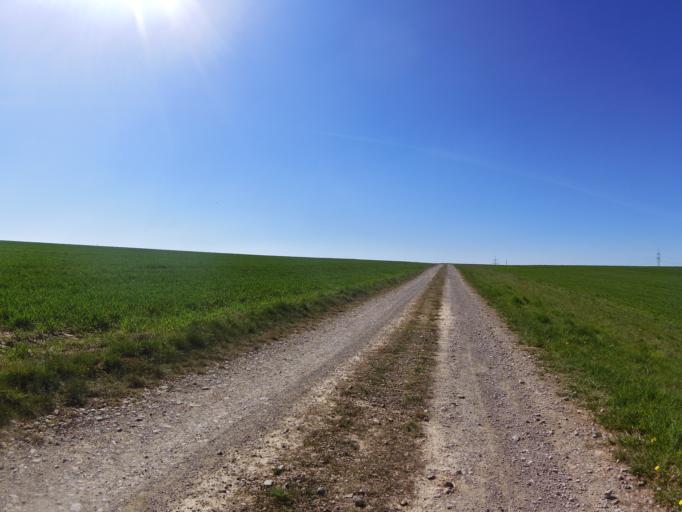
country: DE
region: Bavaria
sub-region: Regierungsbezirk Unterfranken
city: Biebelried
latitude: 49.8052
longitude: 10.0904
